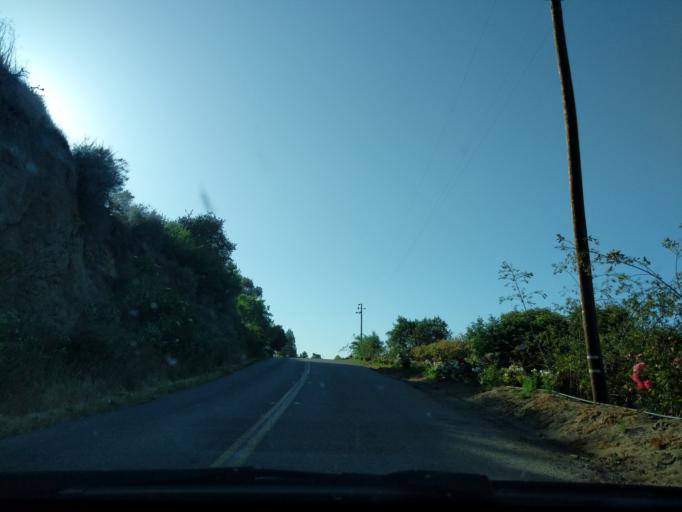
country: US
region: California
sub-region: Monterey County
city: Gonzales
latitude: 36.4810
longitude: -121.4856
